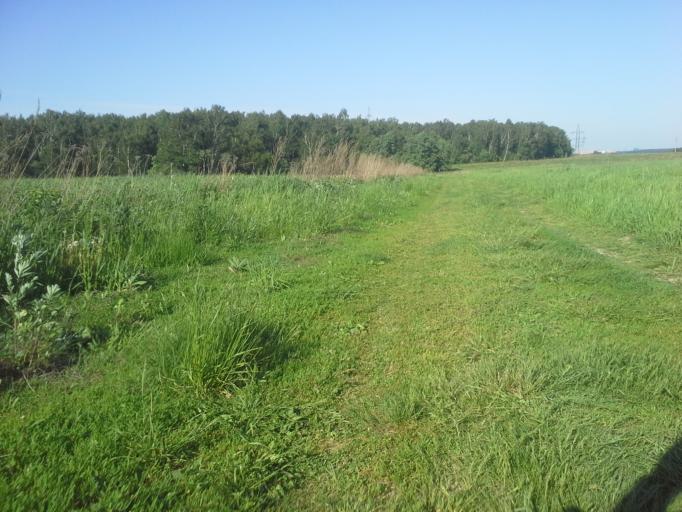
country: RU
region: Moskovskaya
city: Dubrovitsy
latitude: 55.4744
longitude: 37.4223
